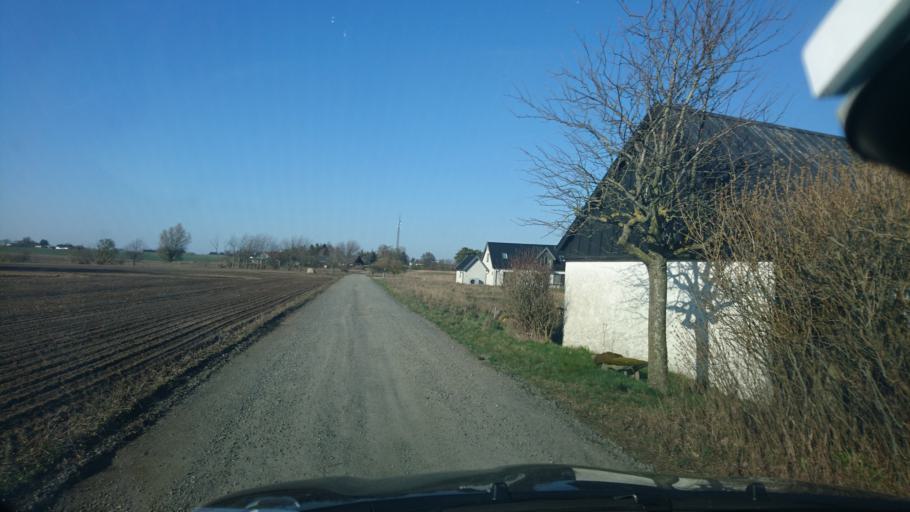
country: SE
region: Skane
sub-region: Simrishamns Kommun
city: Simrishamn
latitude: 55.4174
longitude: 14.2057
